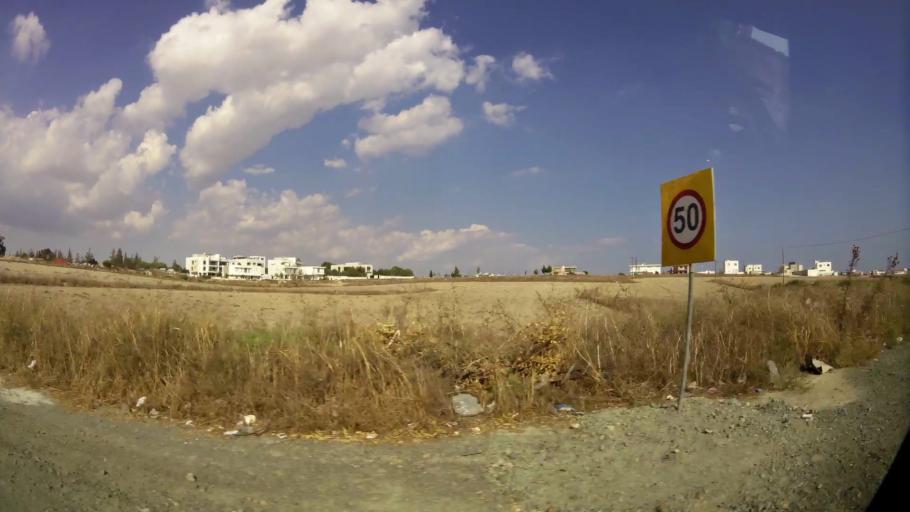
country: CY
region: Larnaka
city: Dhromolaxia
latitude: 34.9057
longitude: 33.5765
